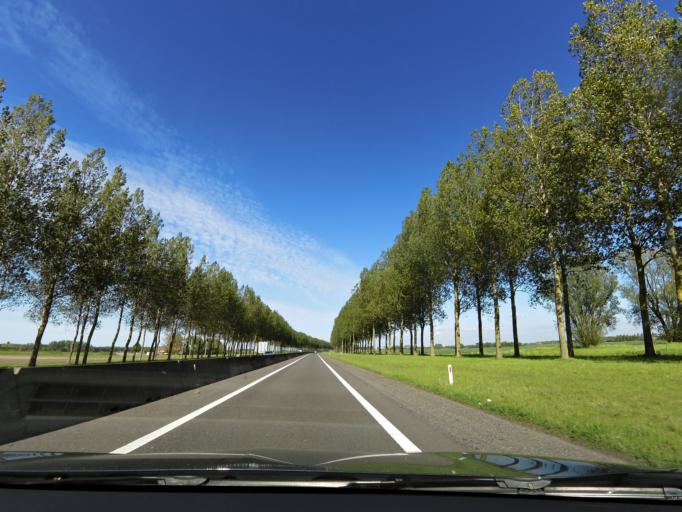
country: NL
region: South Holland
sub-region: Gemeente Hellevoetsluis
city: Nieuw-Helvoet
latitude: 51.8501
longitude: 4.0924
